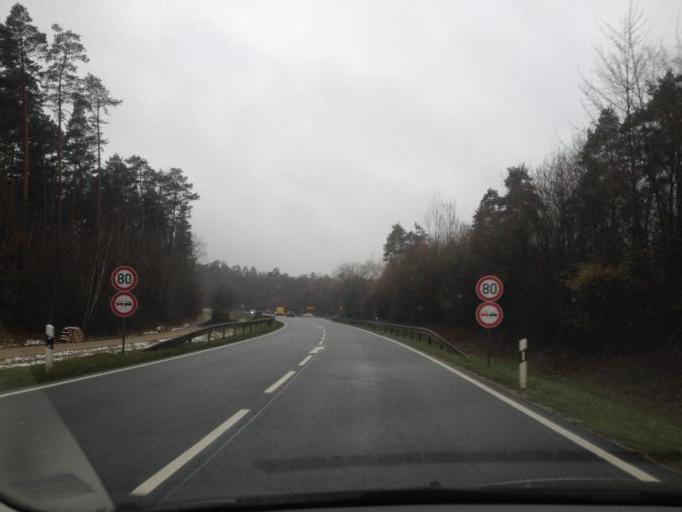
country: DE
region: Bavaria
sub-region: Regierungsbezirk Mittelfranken
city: Heroldsberg
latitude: 49.5210
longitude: 11.1524
